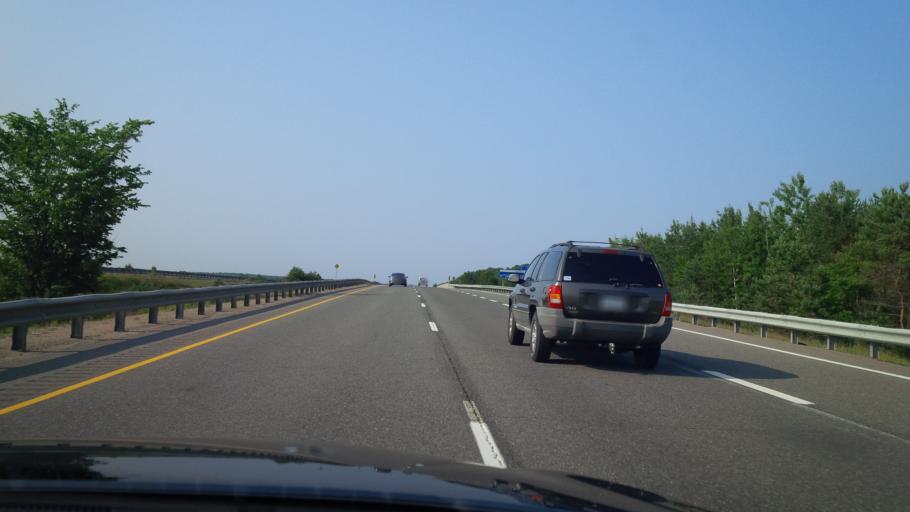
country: CA
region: Ontario
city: Huntsville
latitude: 45.3417
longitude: -79.2334
